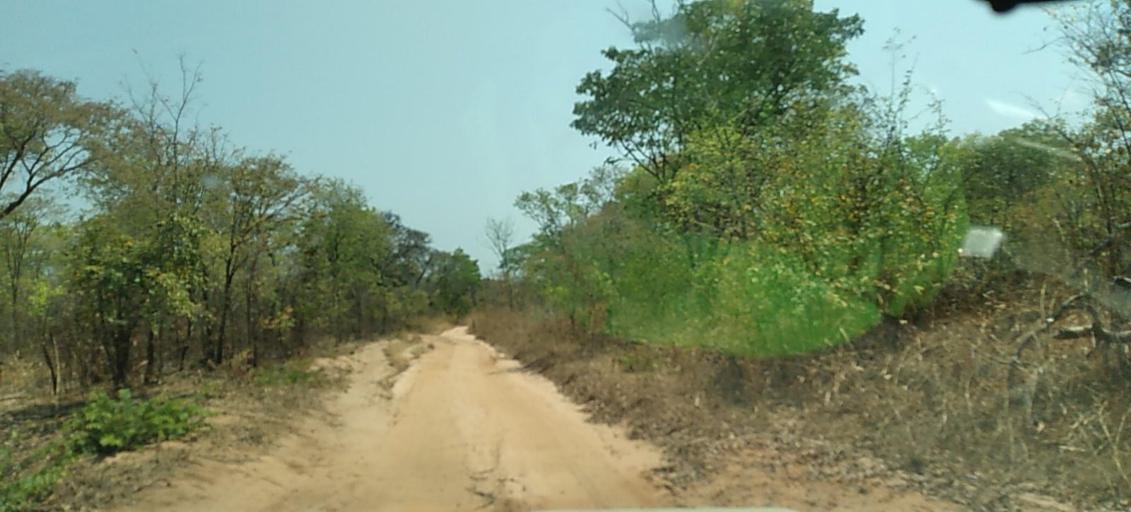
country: ZM
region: North-Western
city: Kalengwa
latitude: -13.1180
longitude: 24.6911
